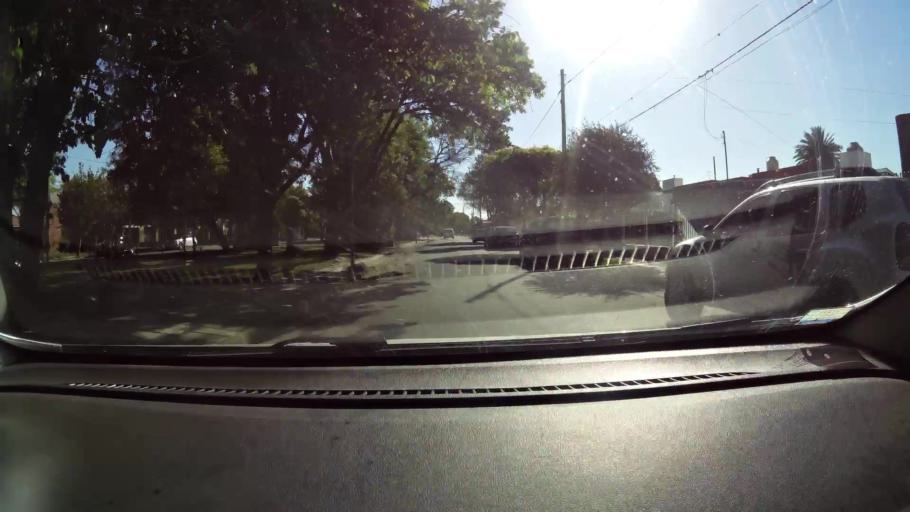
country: AR
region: Cordoba
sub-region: Departamento de Capital
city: Cordoba
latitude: -31.3615
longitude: -64.2120
